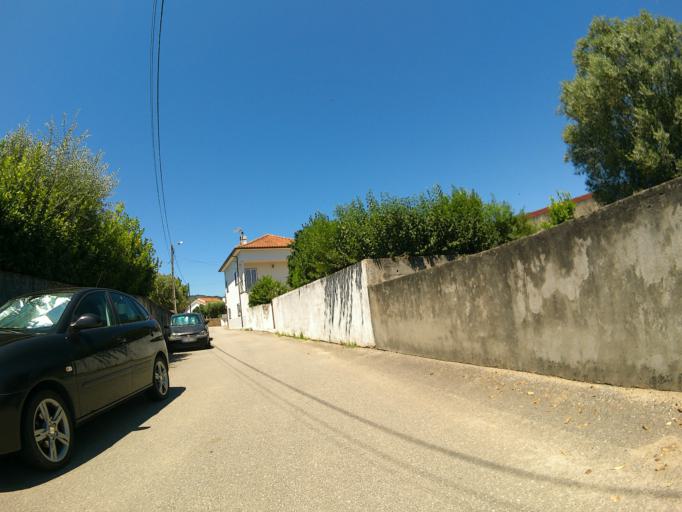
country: PT
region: Viana do Castelo
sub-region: Viana do Castelo
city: Darque
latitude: 41.7149
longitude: -8.7149
